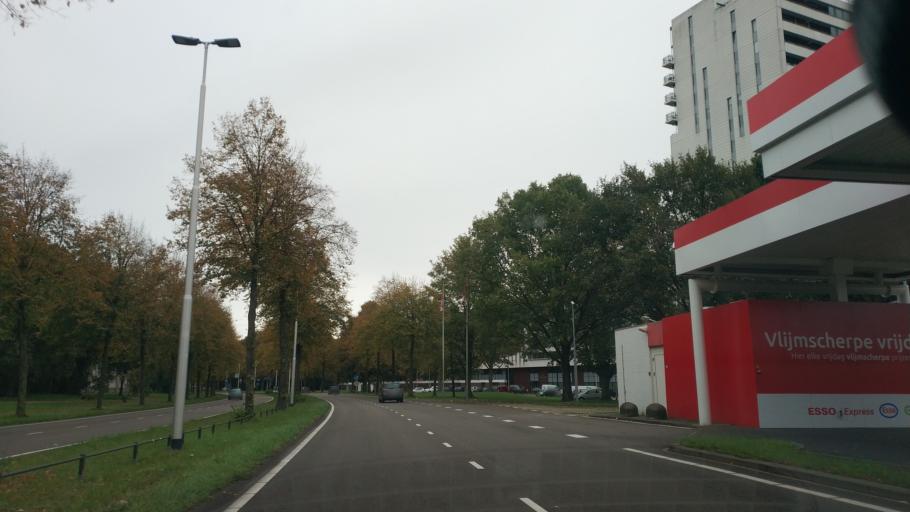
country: NL
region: North Brabant
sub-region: Gemeente Tilburg
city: Tilburg
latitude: 51.5432
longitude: 5.0885
